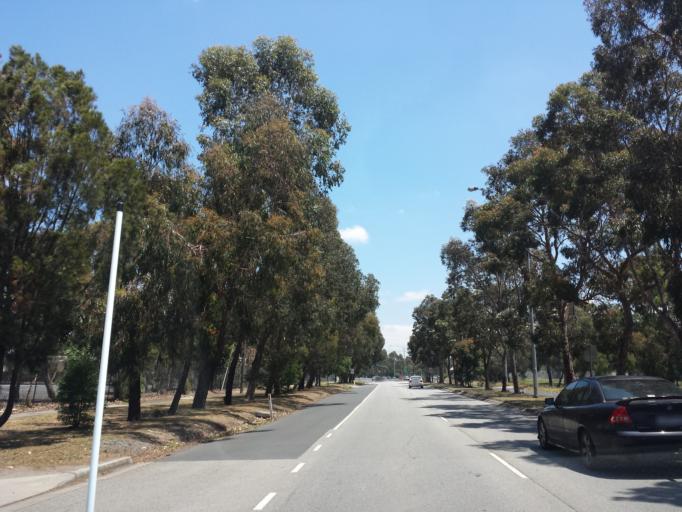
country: AU
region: Victoria
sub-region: Knox
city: Bayswater
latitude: -37.8384
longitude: 145.2746
